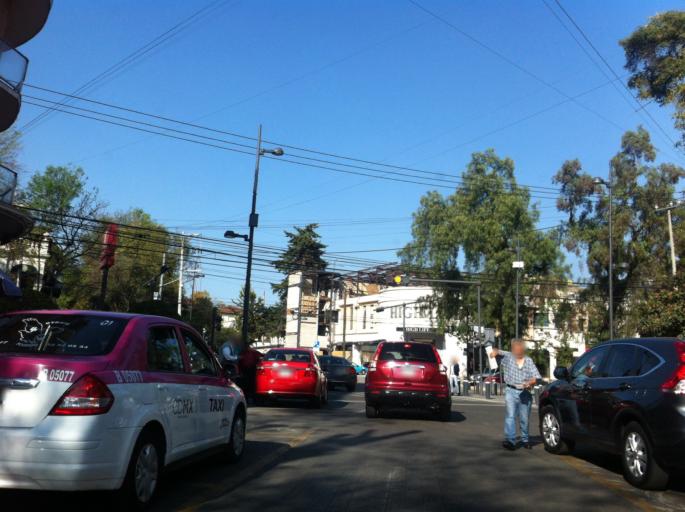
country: MX
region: Mexico City
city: Miguel Hidalgo
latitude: 19.4313
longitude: -99.1960
